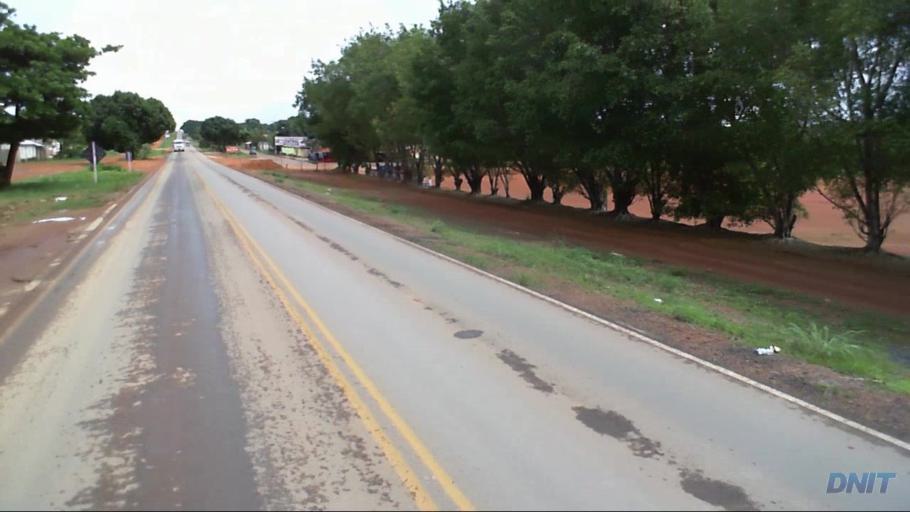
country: BR
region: Goias
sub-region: Padre Bernardo
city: Padre Bernardo
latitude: -15.2641
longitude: -48.2646
